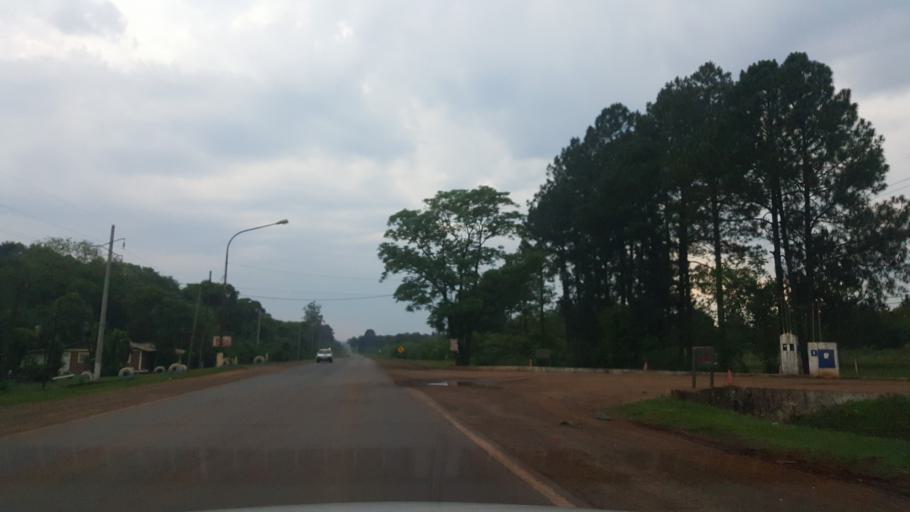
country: AR
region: Misiones
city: Jardin America
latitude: -27.0289
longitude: -55.2149
